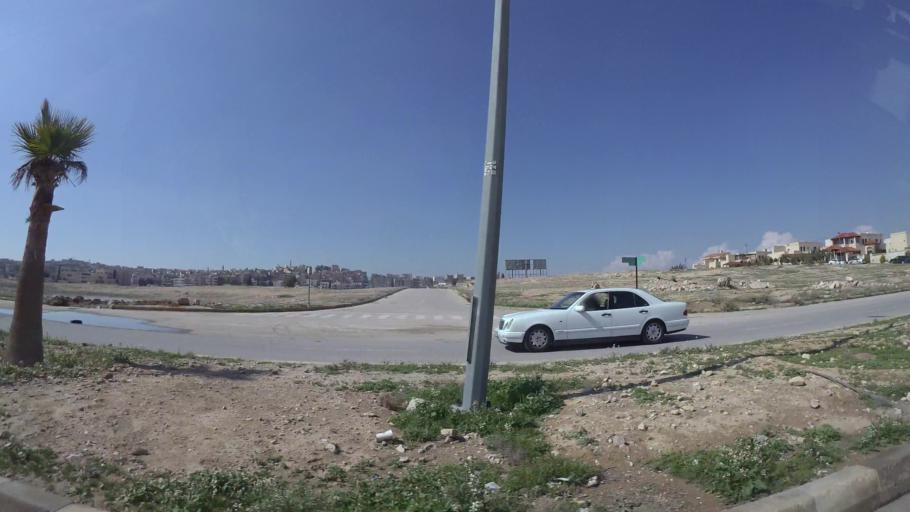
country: JO
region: Zarqa
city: Zarqa
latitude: 32.0761
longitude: 36.1083
